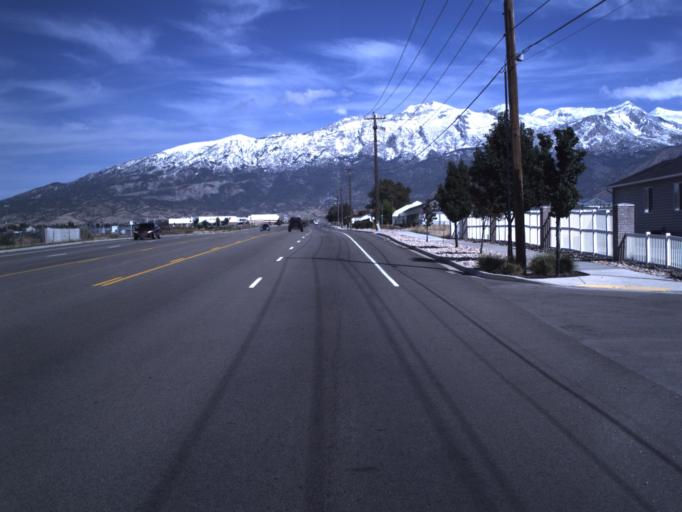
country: US
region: Utah
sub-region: Utah County
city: Cedar Hills
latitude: 40.4067
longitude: -111.7733
